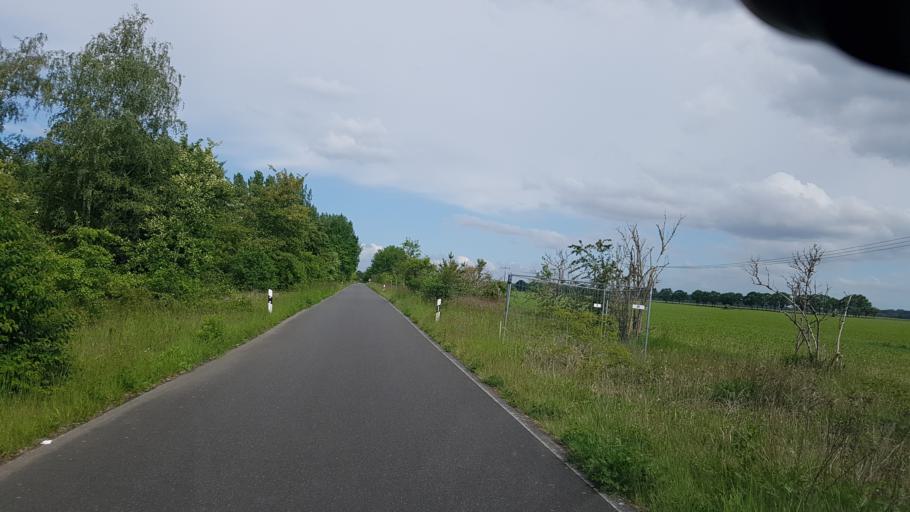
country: DE
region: Brandenburg
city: Crinitz
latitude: 51.8119
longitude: 13.8086
